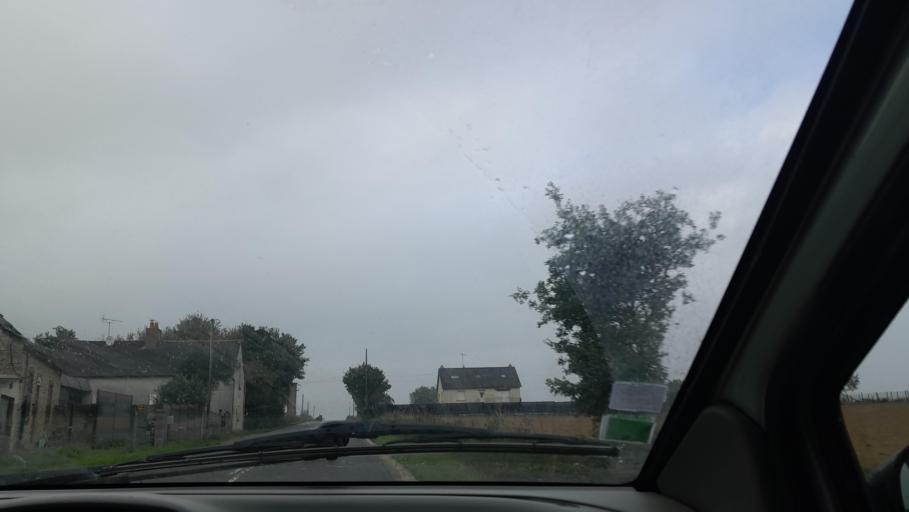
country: FR
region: Pays de la Loire
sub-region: Departement de la Mayenne
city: Congrier
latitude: 47.8133
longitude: -1.1477
